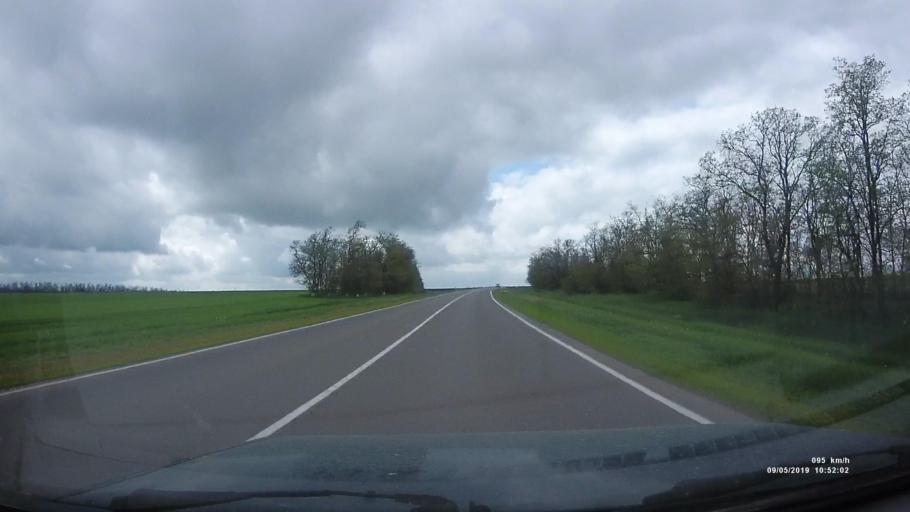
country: RU
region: Rostov
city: Peshkovo
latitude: 46.9064
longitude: 39.3549
